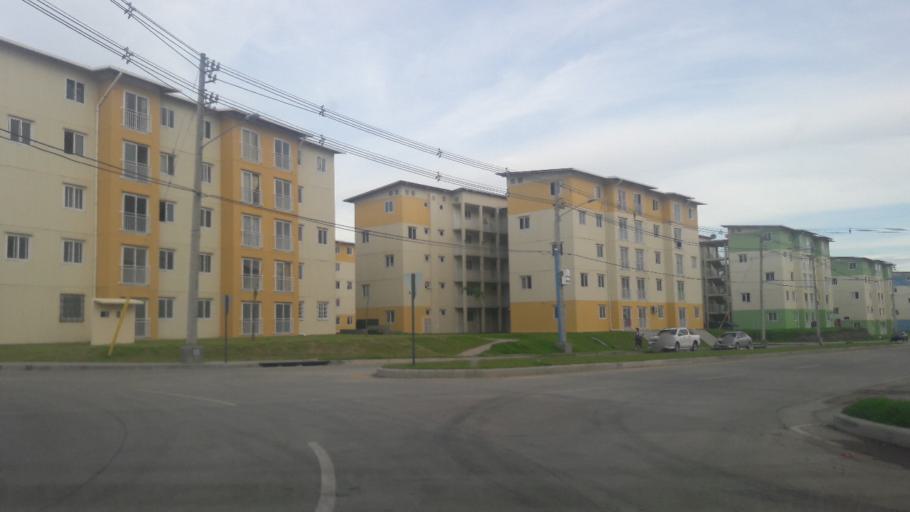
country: PA
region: Colon
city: Cativa
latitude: 9.3709
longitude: -79.8505
